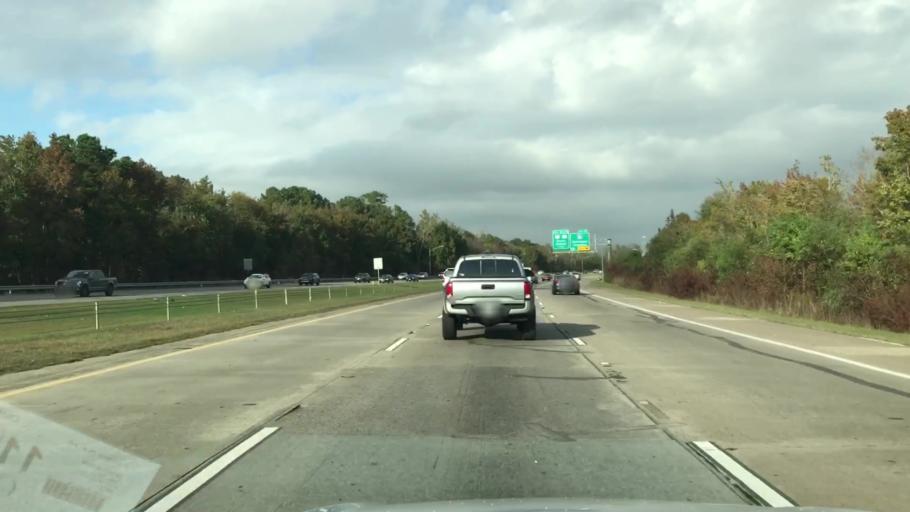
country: US
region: South Carolina
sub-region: Berkeley County
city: Hanahan
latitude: 32.8771
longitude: -80.0258
